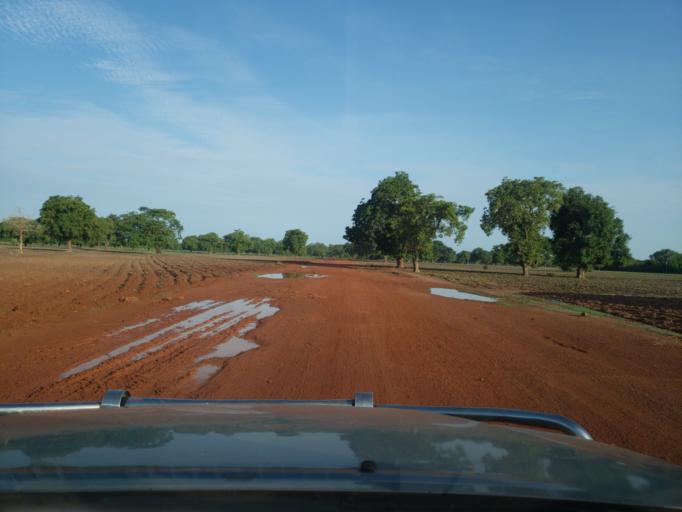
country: ML
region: Sikasso
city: Koutiala
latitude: 12.4073
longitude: -5.5461
